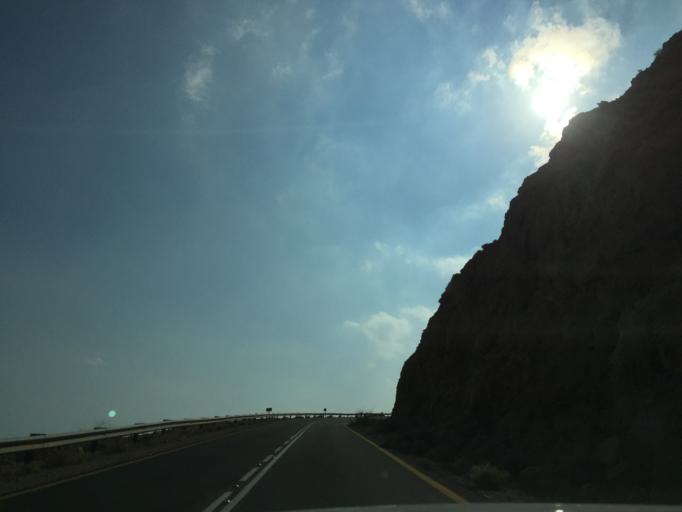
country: IL
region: Southern District
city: `En Boqeq
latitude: 31.3206
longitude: 35.3324
